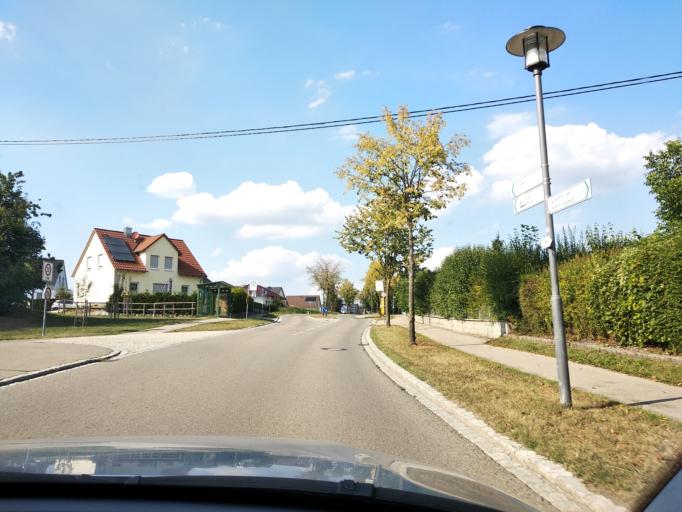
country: DE
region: Bavaria
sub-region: Swabia
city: Ungerhausen
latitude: 48.0093
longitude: 10.2721
